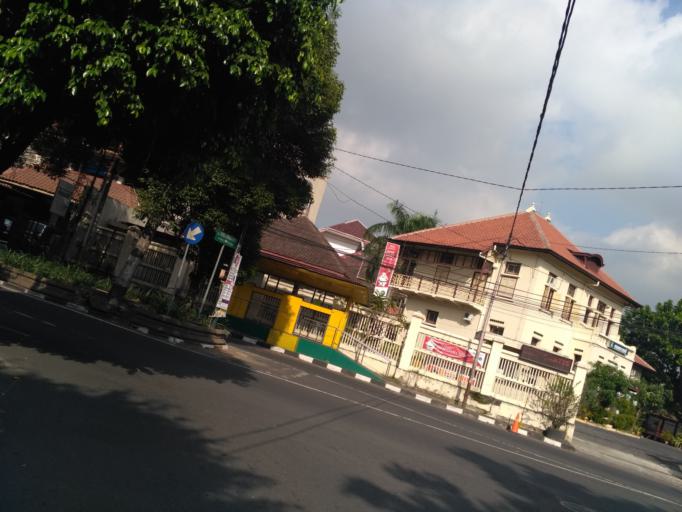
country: ID
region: Daerah Istimewa Yogyakarta
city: Yogyakarta
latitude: -7.7846
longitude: 110.3715
